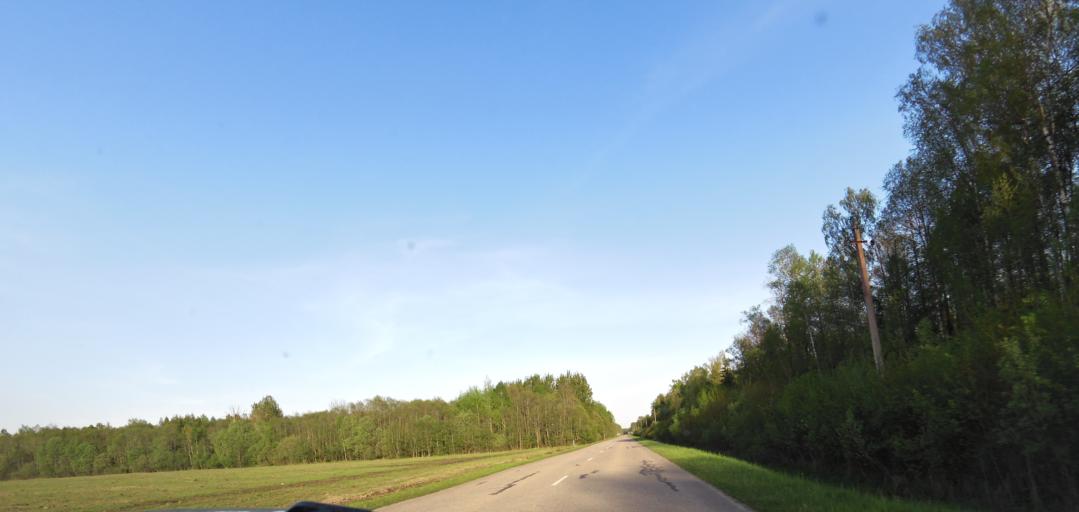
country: LT
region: Vilnius County
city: Ukmerge
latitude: 55.4198
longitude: 24.6137
